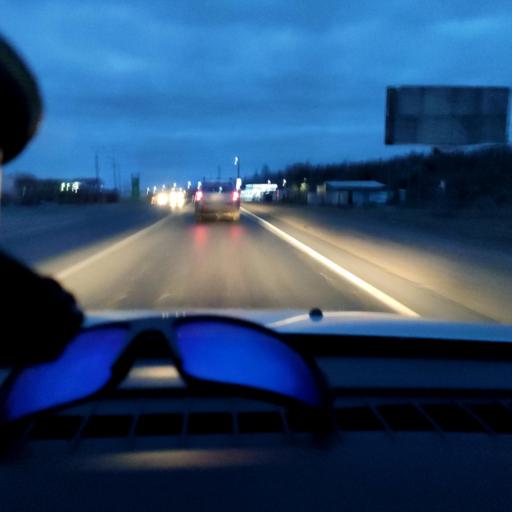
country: RU
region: Samara
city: Novokuybyshevsk
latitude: 53.0828
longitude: 50.0708
